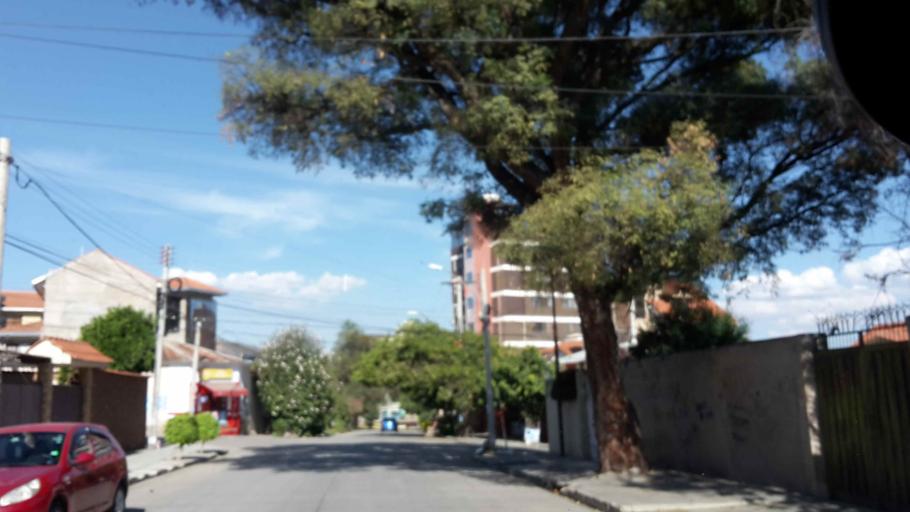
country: BO
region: Cochabamba
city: Cochabamba
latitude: -17.3662
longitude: -66.1613
